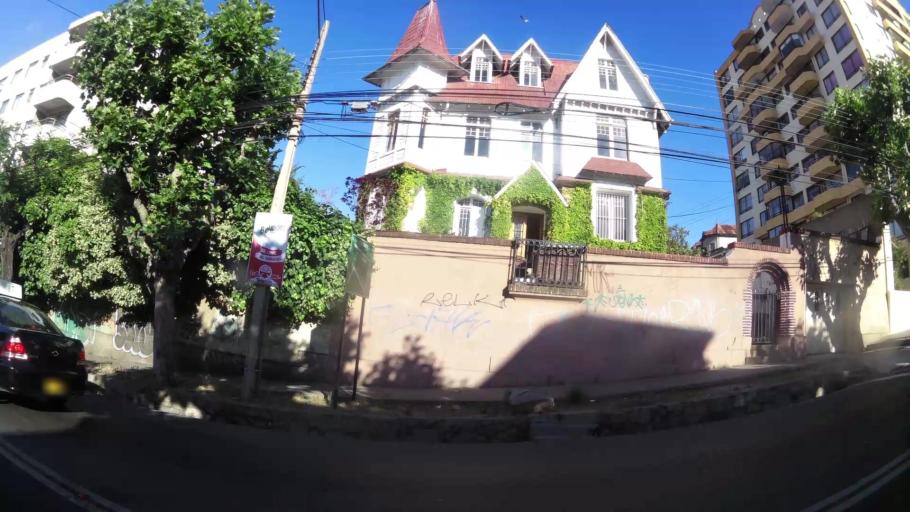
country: CL
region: Valparaiso
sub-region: Provincia de Valparaiso
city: Vina del Mar
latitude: -33.0293
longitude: -71.5634
